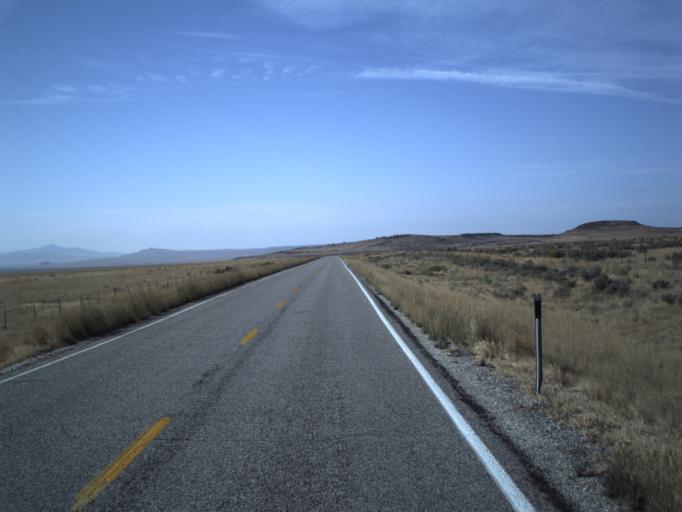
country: US
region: Idaho
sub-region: Minidoka County
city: Rupert
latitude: 41.8606
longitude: -113.1288
